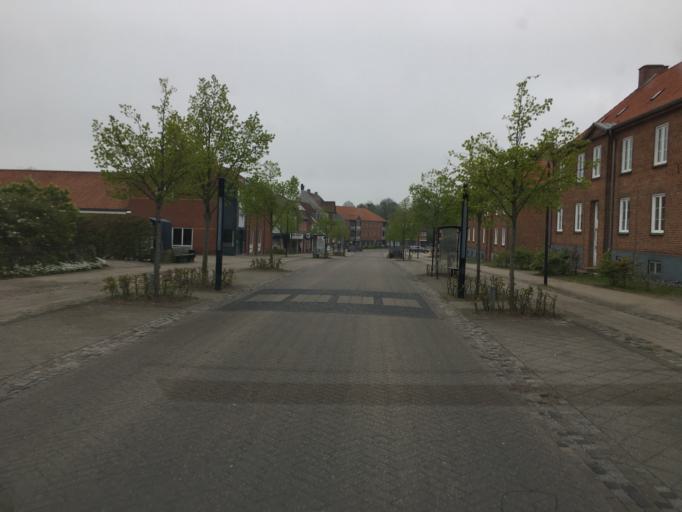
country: DK
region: South Denmark
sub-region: Aabenraa Kommune
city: Padborg
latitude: 54.8220
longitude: 9.3618
